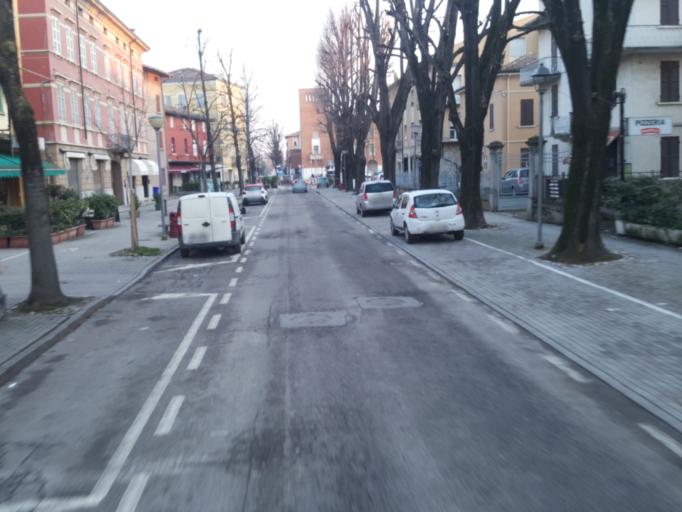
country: IT
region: Emilia-Romagna
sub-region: Provincia di Parma
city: Sorbolo
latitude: 44.8450
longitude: 10.4479
